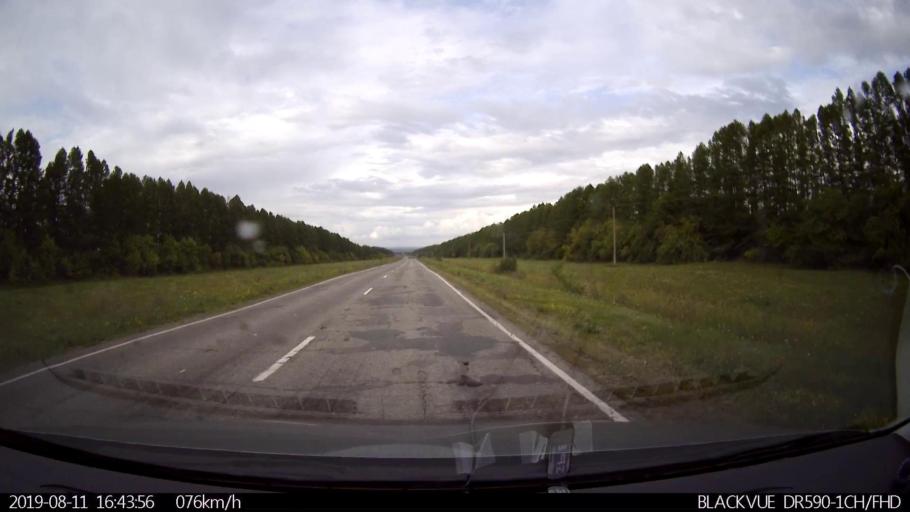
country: RU
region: Ulyanovsk
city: Mayna
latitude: 54.1740
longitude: 47.6768
